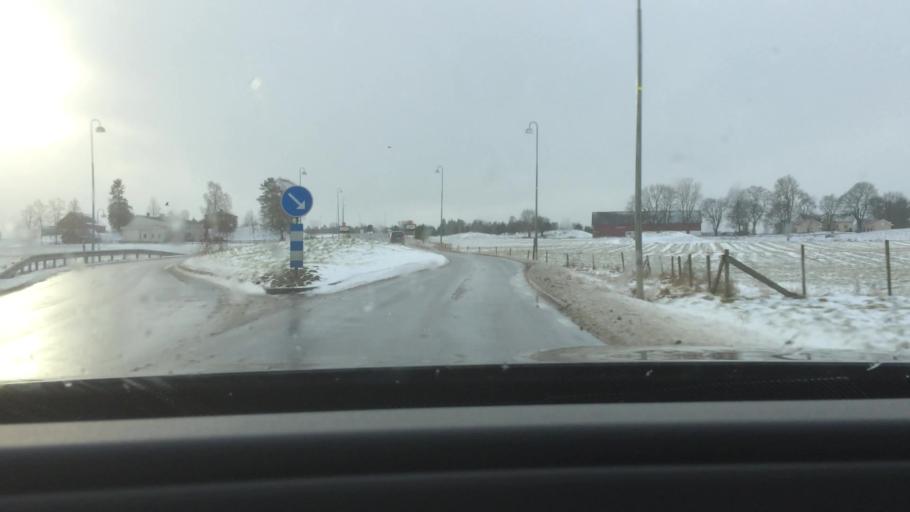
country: SE
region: Vaestra Goetaland
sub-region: Falkopings Kommun
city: Falkoeping
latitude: 57.9826
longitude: 13.5298
